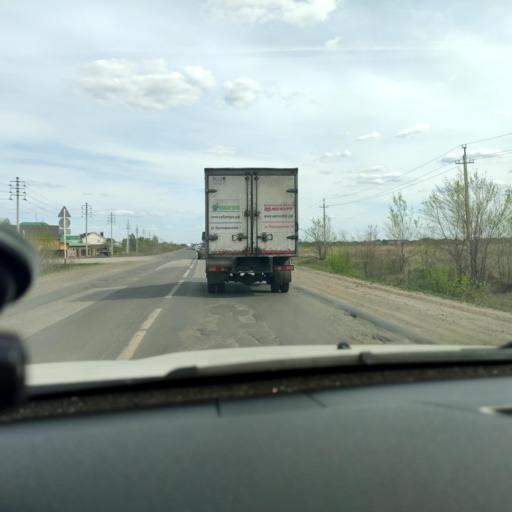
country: RU
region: Samara
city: Kinel'
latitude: 53.2196
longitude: 50.6060
